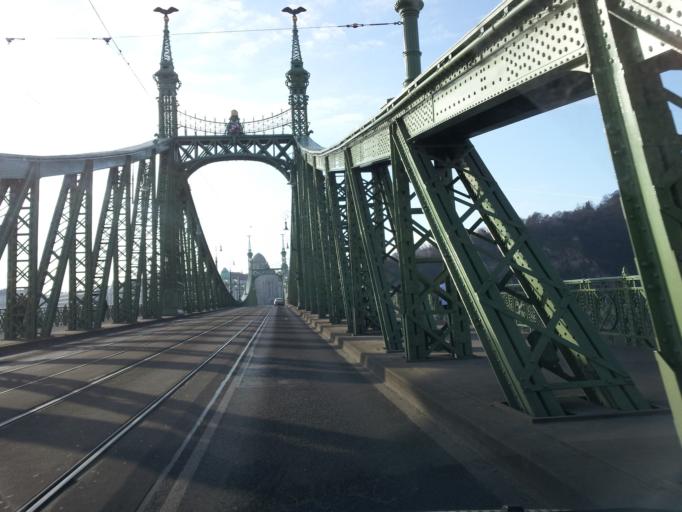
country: HU
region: Budapest
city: Budapest IX. keruelet
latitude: 47.4861
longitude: 19.0561
